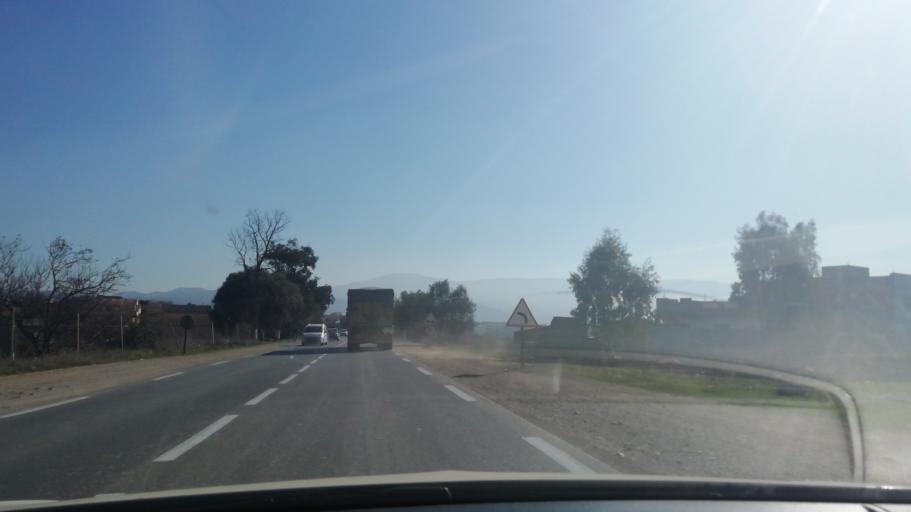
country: DZ
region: Tlemcen
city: Nedroma
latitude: 35.0780
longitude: -1.7884
